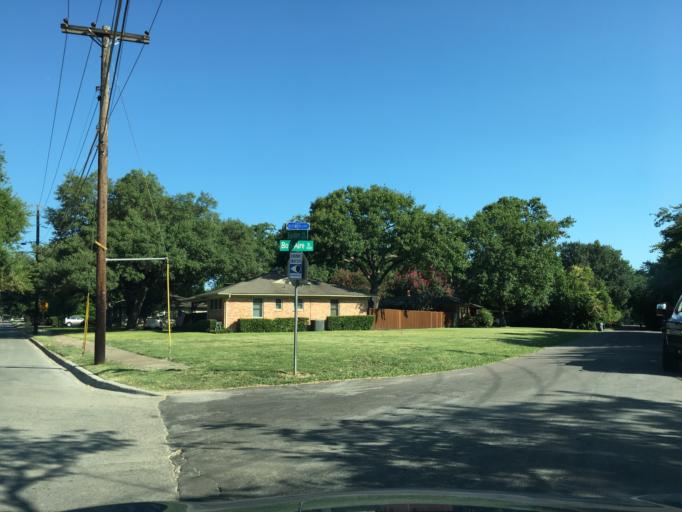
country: US
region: Texas
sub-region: Dallas County
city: Garland
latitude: 32.8584
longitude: -96.7057
